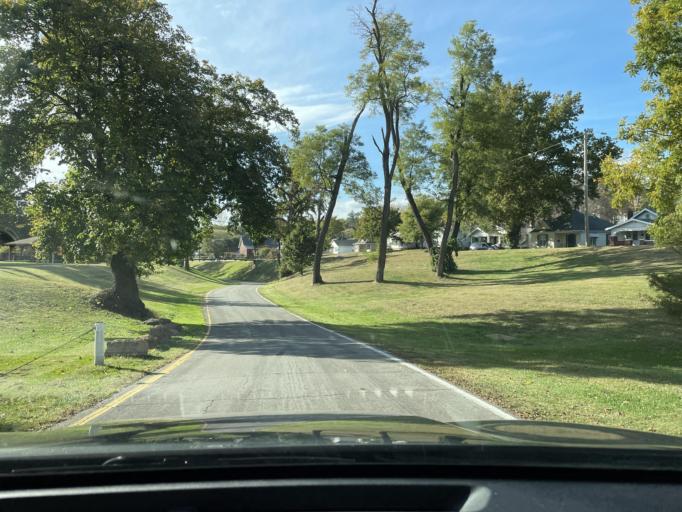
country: US
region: Kansas
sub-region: Doniphan County
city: Elwood
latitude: 39.7112
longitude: -94.8515
